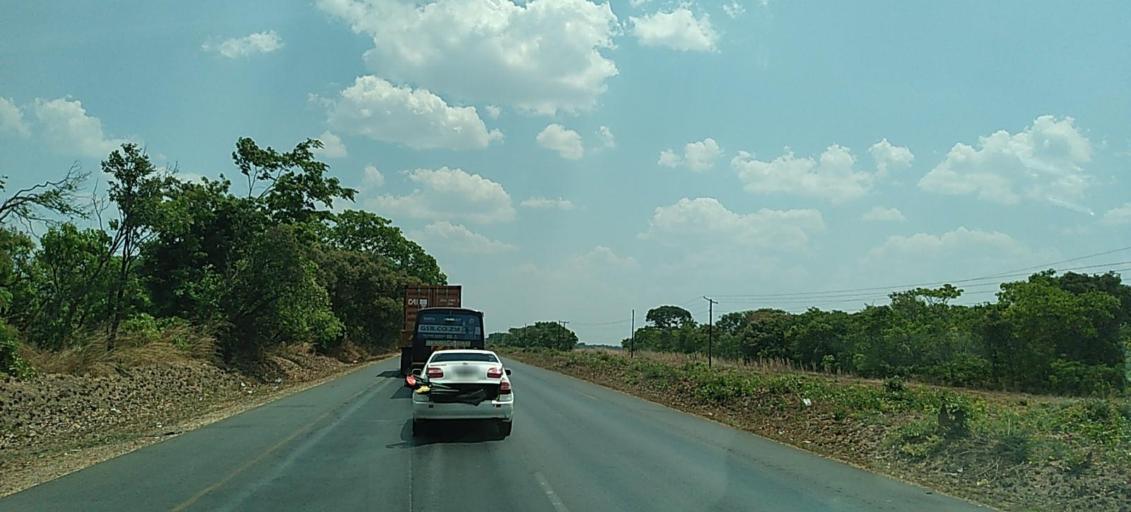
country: ZM
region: Central
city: Kabwe
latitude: -14.3356
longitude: 28.5327
